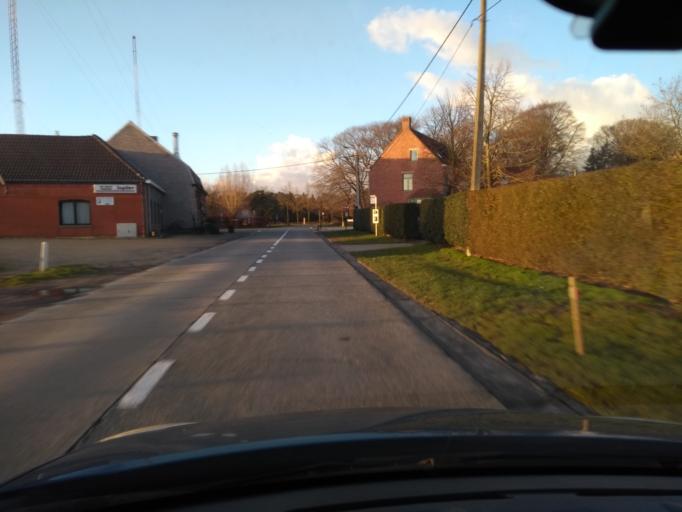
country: BE
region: Flanders
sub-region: Provincie West-Vlaanderen
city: Ruiselede
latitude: 51.0806
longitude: 3.3496
